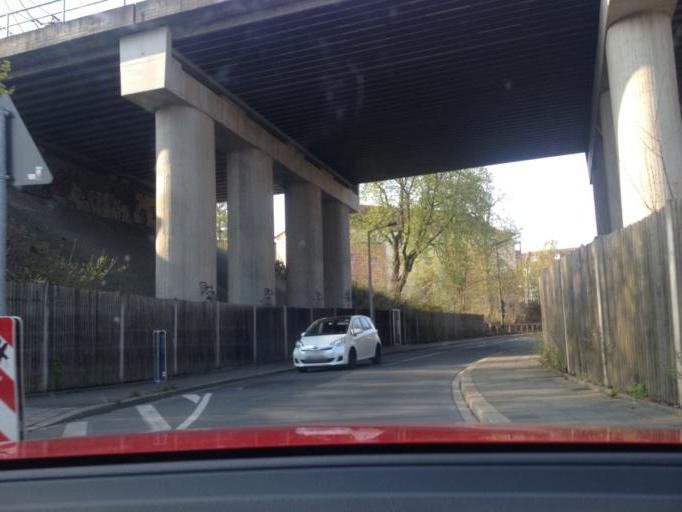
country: DE
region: Bavaria
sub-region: Regierungsbezirk Mittelfranken
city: Nuernberg
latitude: 49.4478
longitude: 11.1055
